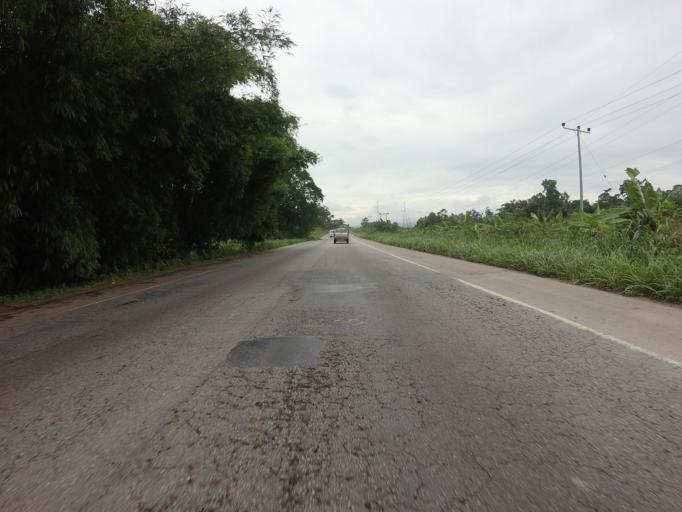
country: GH
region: Eastern
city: Begoro
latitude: 6.4110
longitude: -0.5694
